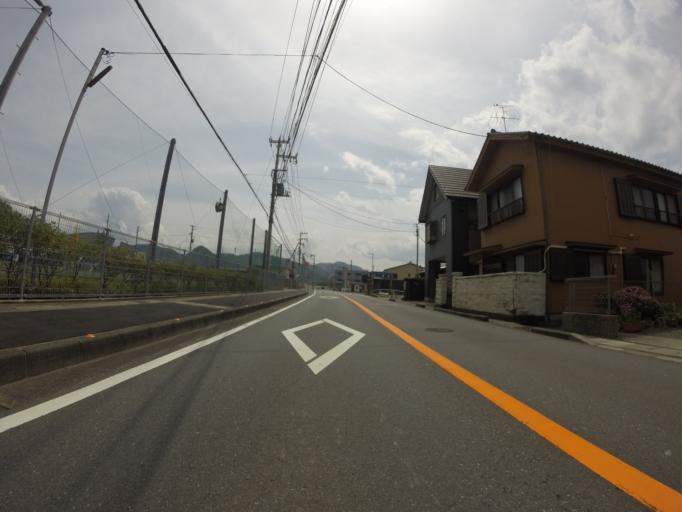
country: JP
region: Shizuoka
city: Numazu
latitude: 35.0506
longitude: 138.8854
